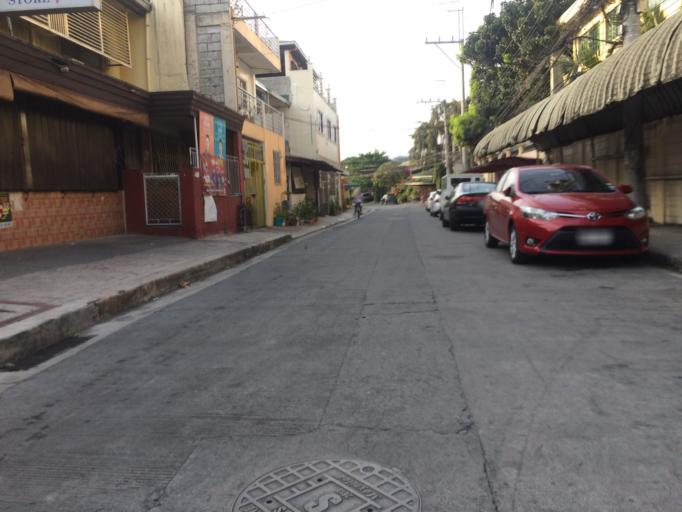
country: PH
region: Calabarzon
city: Bagong Pagasa
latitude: 14.6755
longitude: 121.0226
